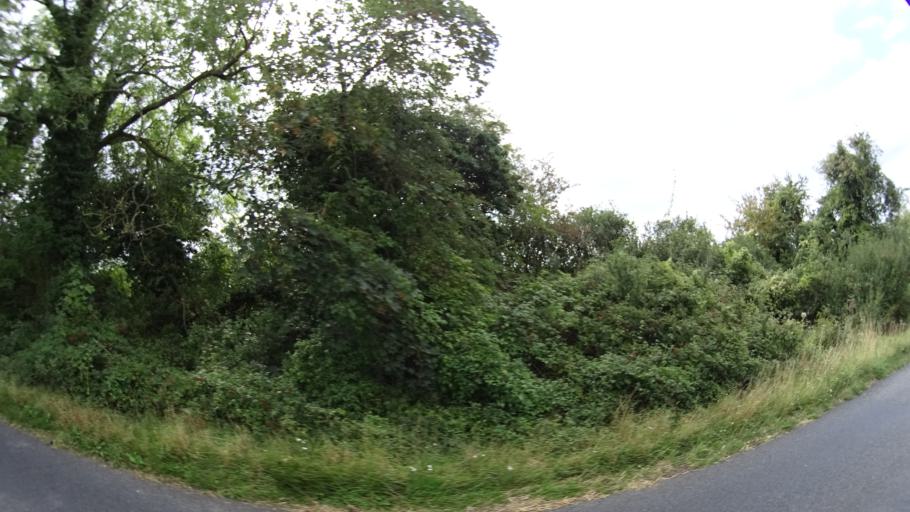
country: GB
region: England
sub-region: Wiltshire
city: Tidworth
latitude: 51.1853
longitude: -1.6531
